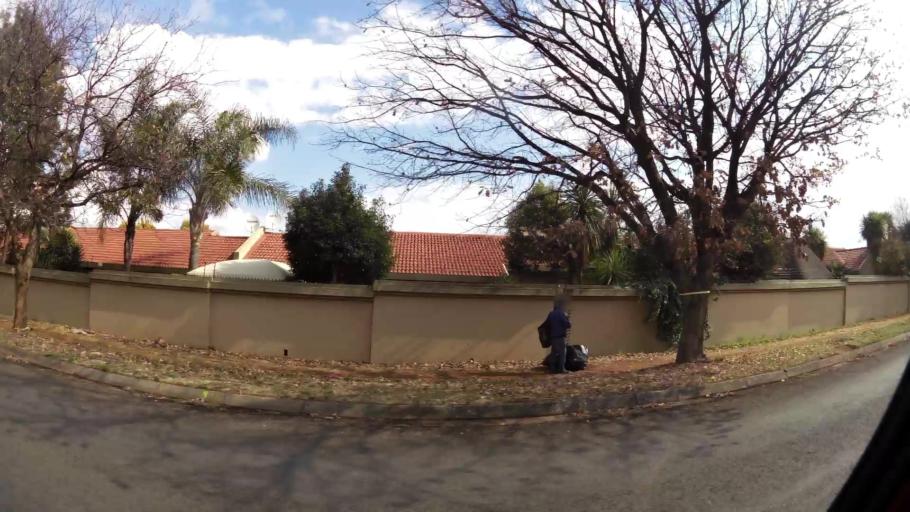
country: ZA
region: Gauteng
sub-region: Sedibeng District Municipality
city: Vanderbijlpark
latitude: -26.7367
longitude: 27.8434
